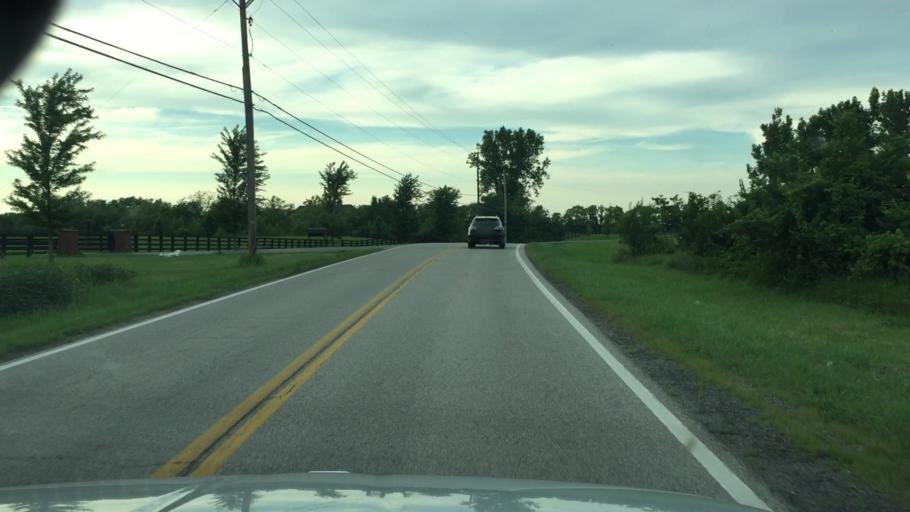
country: US
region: Ohio
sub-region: Madison County
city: West Jefferson
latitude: 39.9842
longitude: -83.2639
